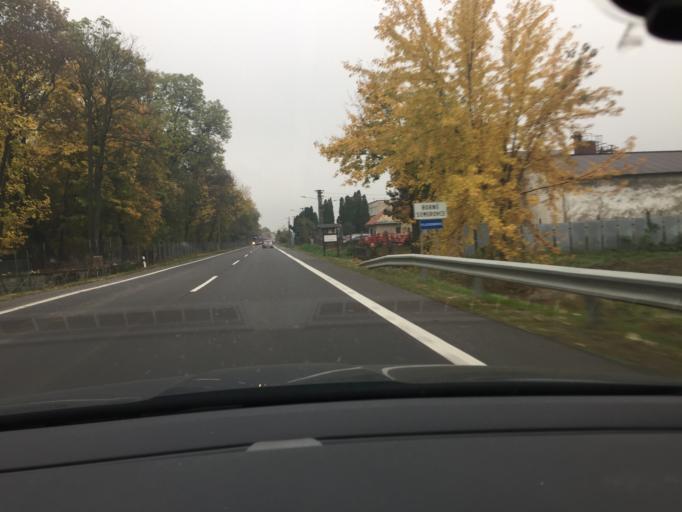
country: SK
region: Banskobystricky
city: Dudince
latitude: 48.1302
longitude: 18.8770
